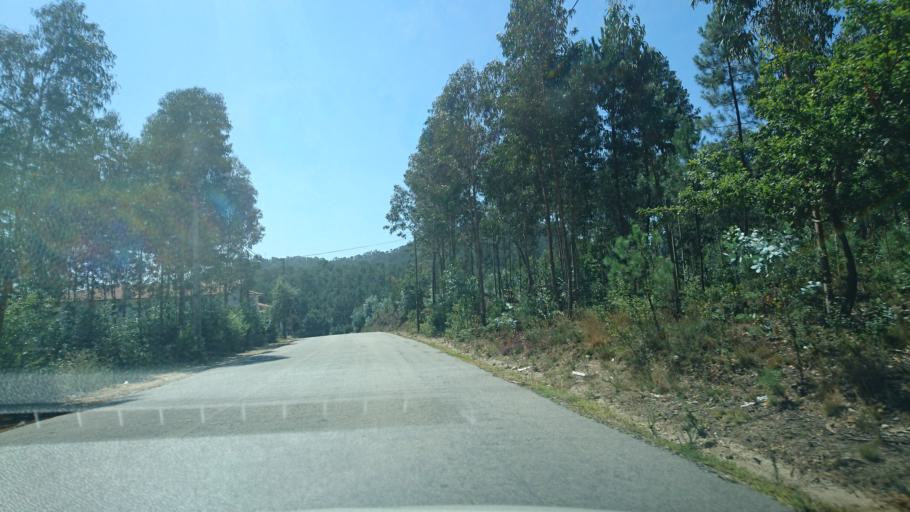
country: PT
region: Aveiro
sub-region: Oliveira de Azemeis
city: Vila Cha
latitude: 40.8815
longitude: -8.4283
